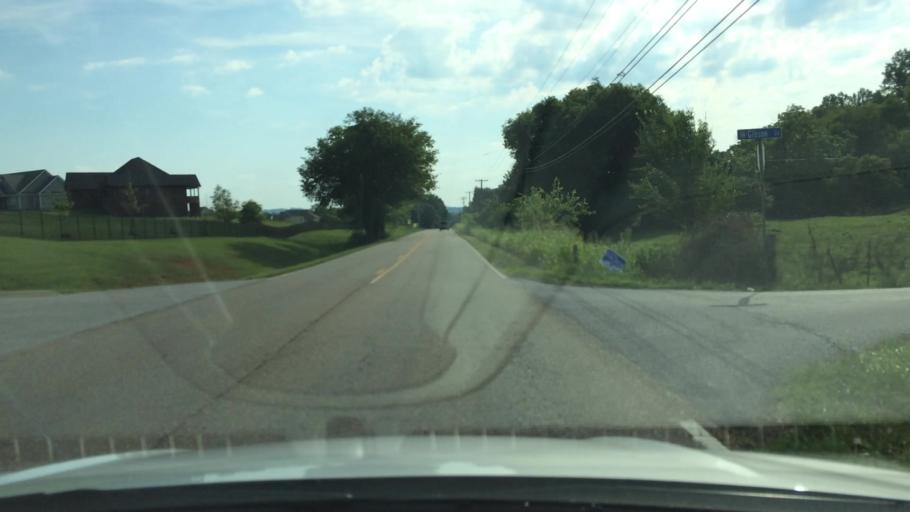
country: US
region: Tennessee
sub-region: Sevier County
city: Seymour
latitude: 35.9091
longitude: -83.6871
